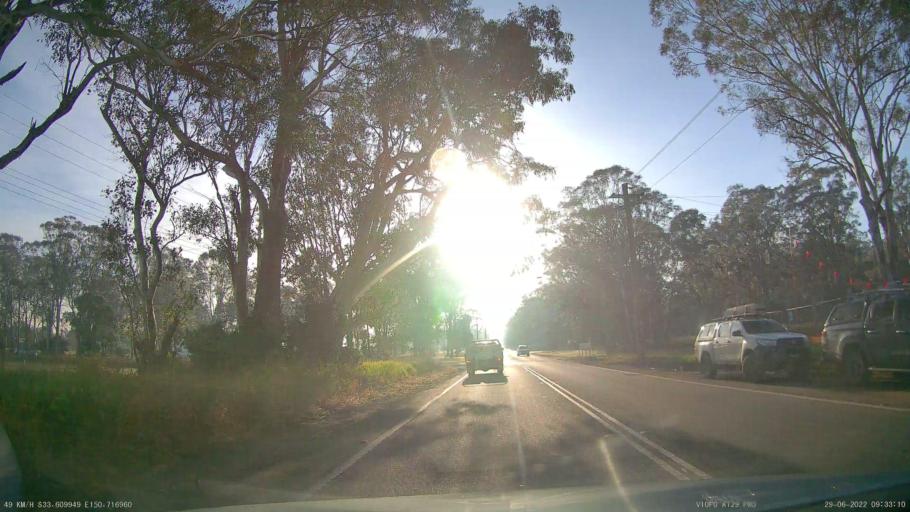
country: AU
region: New South Wales
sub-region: Hawkesbury
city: Richmond
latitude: -33.6097
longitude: 150.7173
